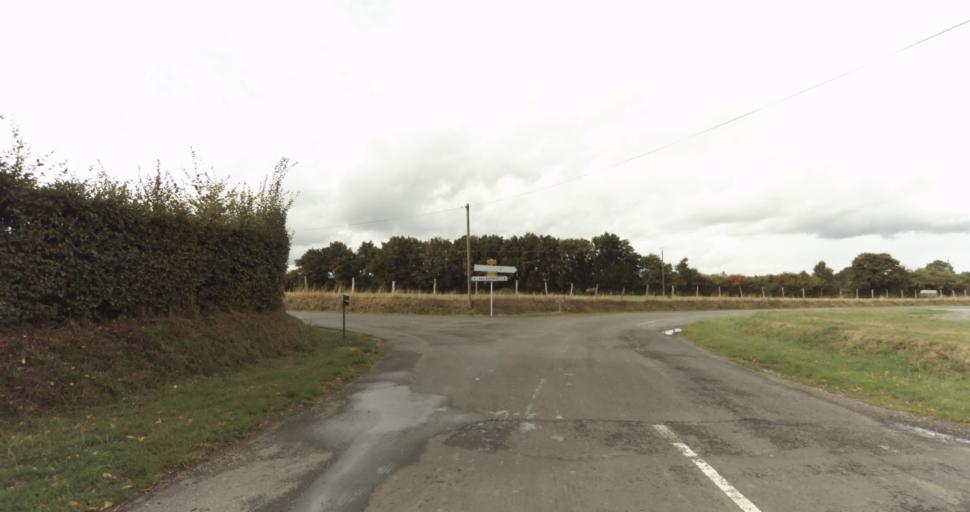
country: FR
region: Lower Normandy
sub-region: Departement de l'Orne
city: Sainte-Gauburge-Sainte-Colombe
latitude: 48.7015
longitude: 0.3672
